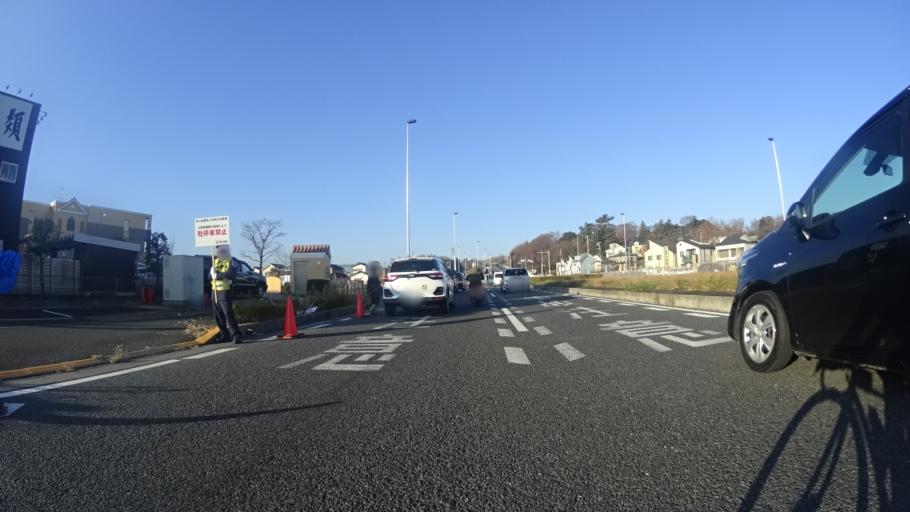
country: JP
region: Tokyo
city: Hino
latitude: 35.6691
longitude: 139.4026
